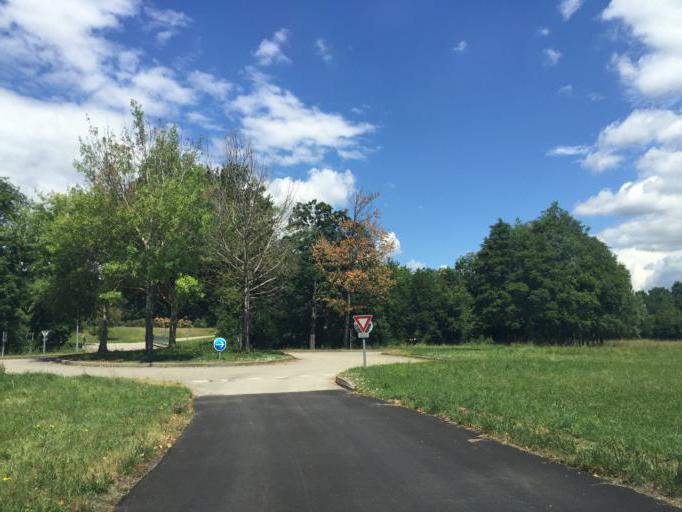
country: FR
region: Rhone-Alpes
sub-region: Departement de la Drome
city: Mercurol
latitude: 45.0780
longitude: 4.8731
